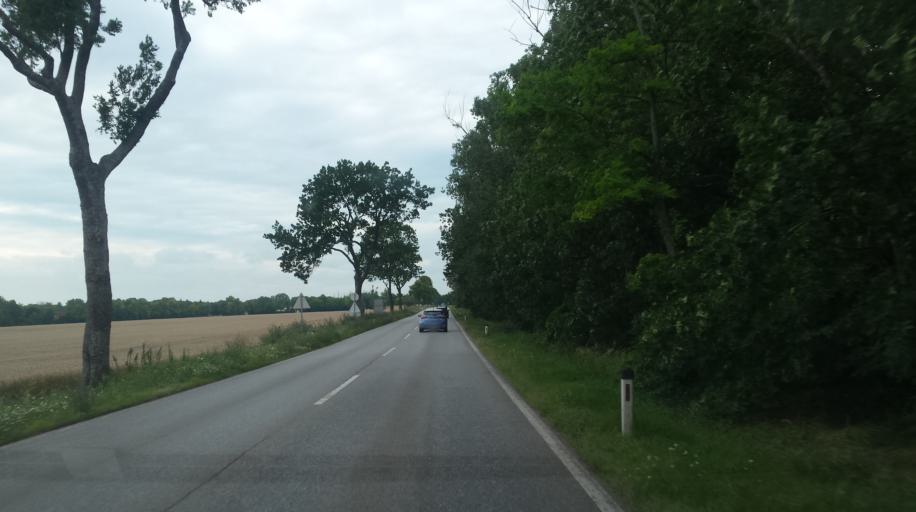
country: AT
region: Lower Austria
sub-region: Politischer Bezirk Wien-Umgebung
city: Moosbrunn
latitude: 48.0534
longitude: 16.4606
